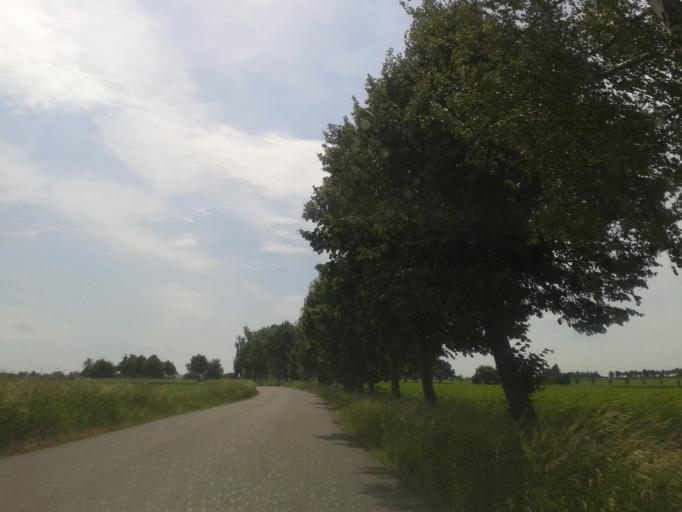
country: DE
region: Saxony
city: Bannewitz
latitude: 50.9909
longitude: 13.7298
